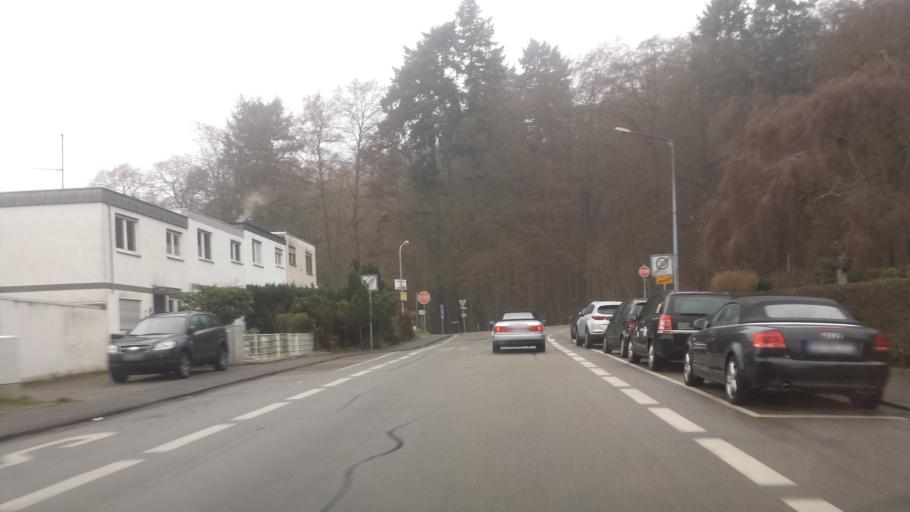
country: DE
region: Hesse
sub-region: Regierungsbezirk Darmstadt
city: Darmstadt
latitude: 49.8395
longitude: 8.6897
